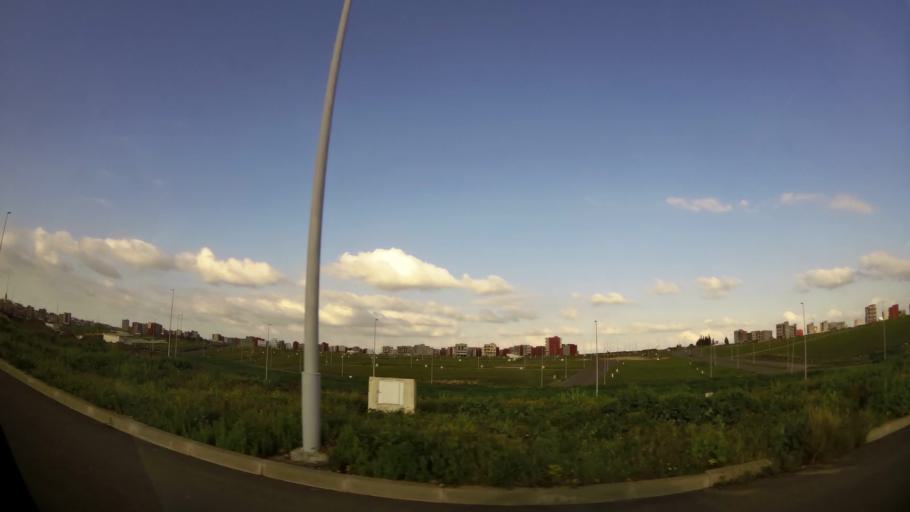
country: MA
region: Chaouia-Ouardigha
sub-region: Settat Province
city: Settat
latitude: 32.9861
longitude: -7.6432
